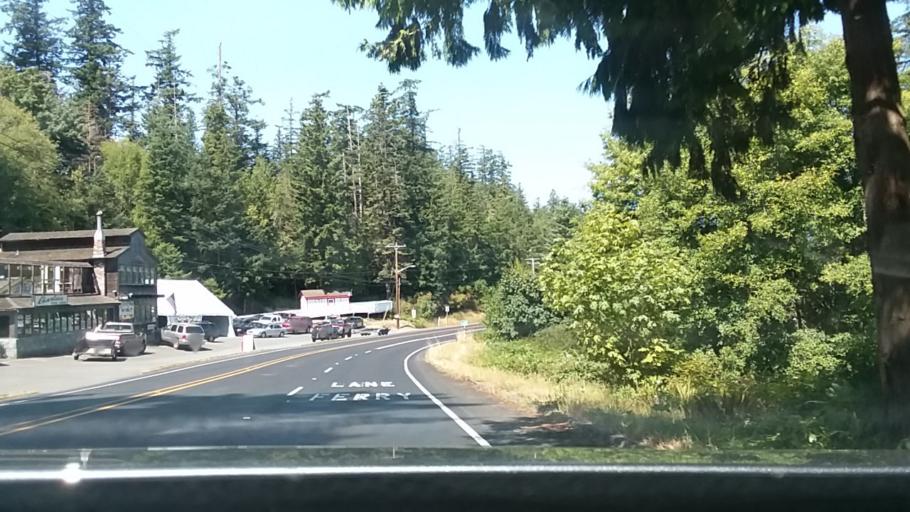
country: US
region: Washington
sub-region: Skagit County
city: Anacortes
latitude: 48.5008
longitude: -122.6785
